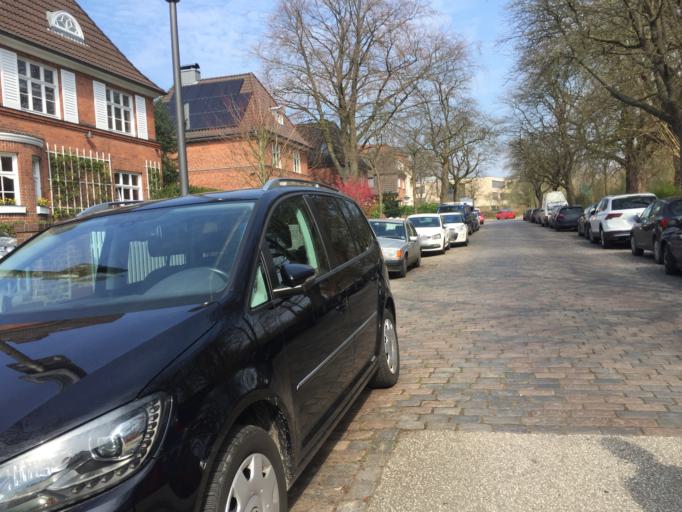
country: DE
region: Schleswig-Holstein
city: Kiel
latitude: 54.3395
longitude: 10.1284
